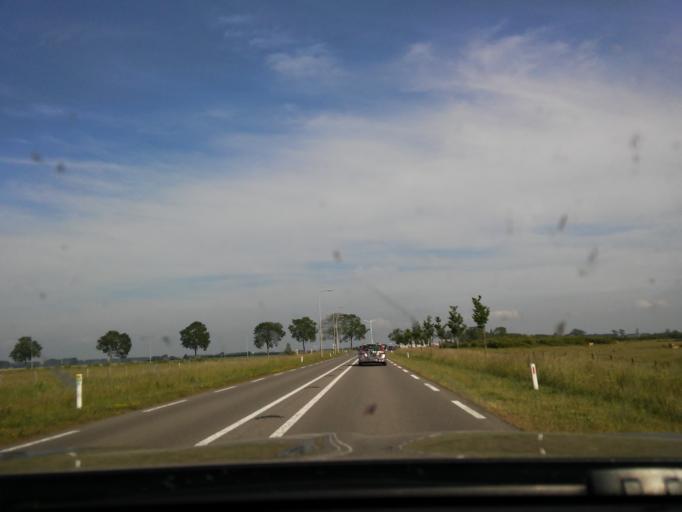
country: NL
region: Zeeland
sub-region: Gemeente Sluis
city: Sluis
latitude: 51.2961
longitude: 3.4228
